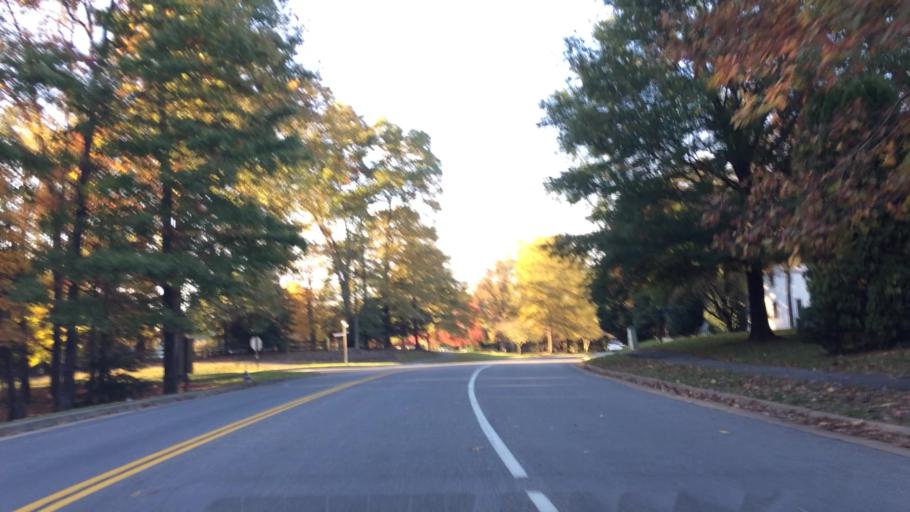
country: US
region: Virginia
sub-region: Henrico County
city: Chamberlayne
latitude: 37.6877
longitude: -77.4285
